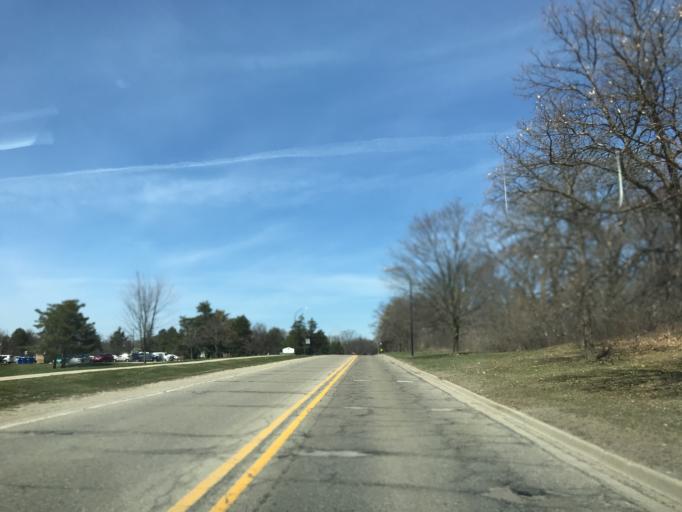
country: US
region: Michigan
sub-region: Washtenaw County
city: Ann Arbor
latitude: 42.3064
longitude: -83.7077
